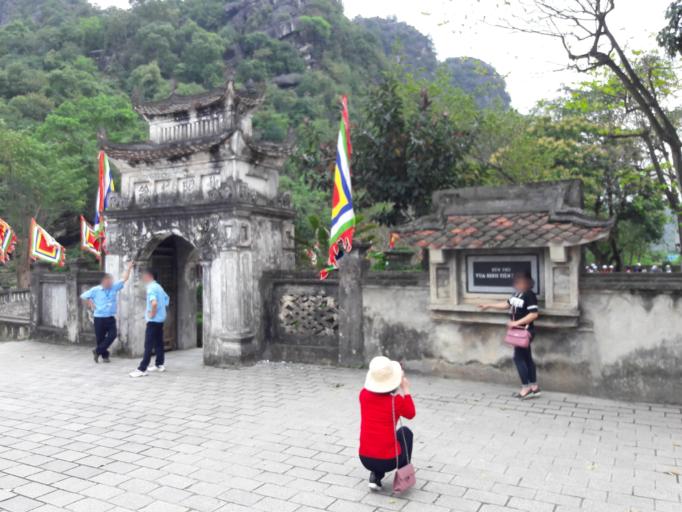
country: VN
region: Ninh Binh
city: Thi Tran Thien Ton
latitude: 20.2846
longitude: 105.9063
